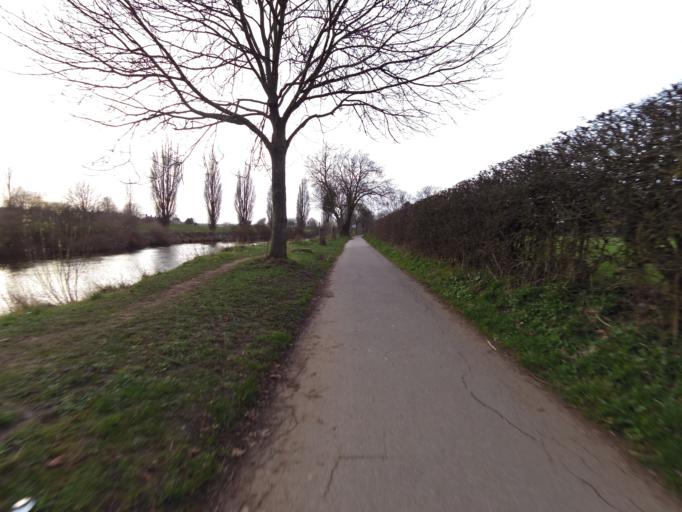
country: GB
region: England
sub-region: City of York
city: York
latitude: 53.9654
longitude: -1.1009
